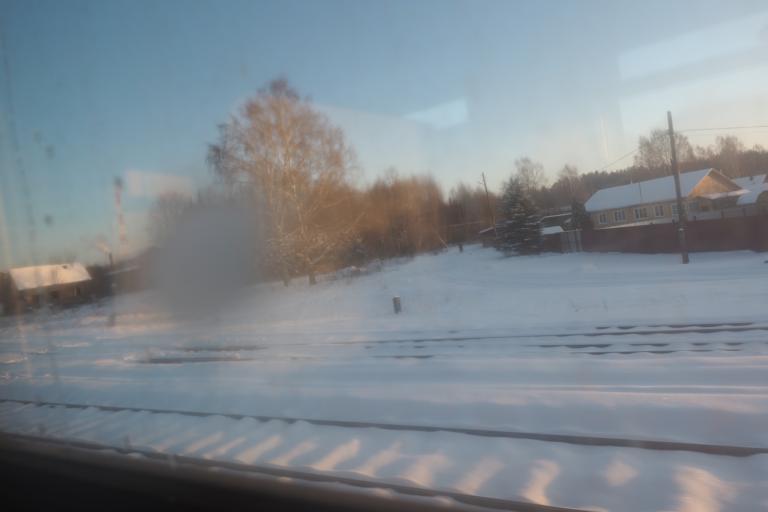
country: RU
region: Tverskaya
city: Ves'yegonsk
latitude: 58.6521
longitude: 37.2581
